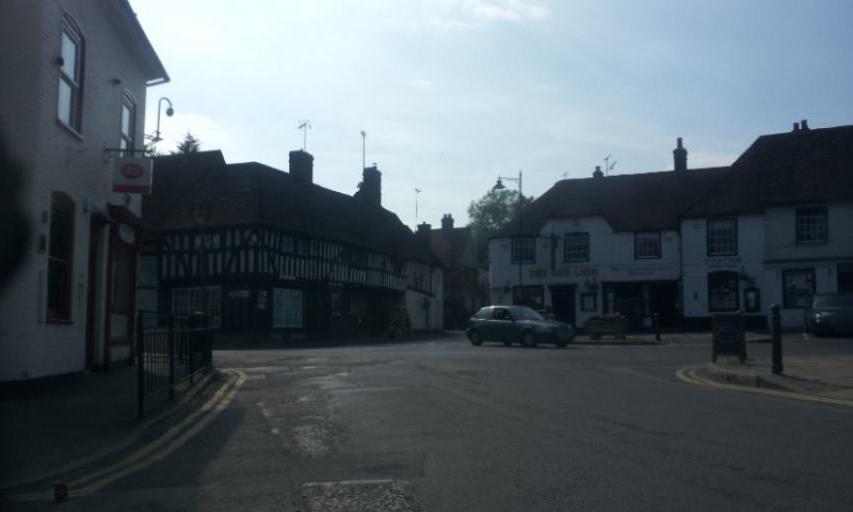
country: GB
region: England
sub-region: Kent
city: Lenham
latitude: 51.2370
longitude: 0.7183
